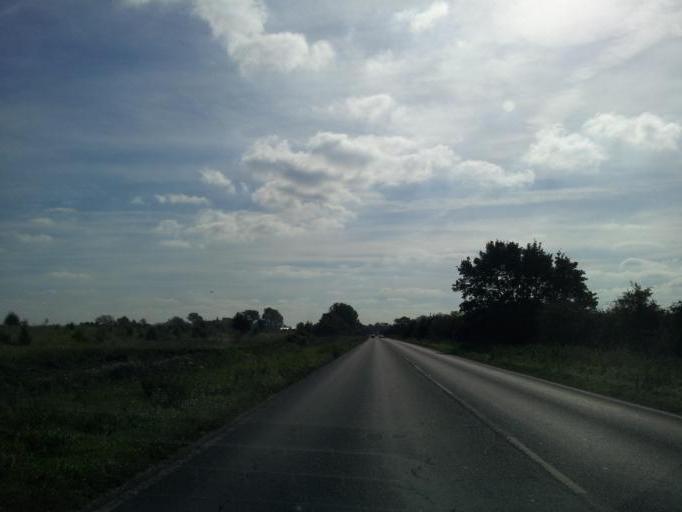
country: GB
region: England
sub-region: Cambridgeshire
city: Waterbeach
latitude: 52.2767
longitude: 0.1738
